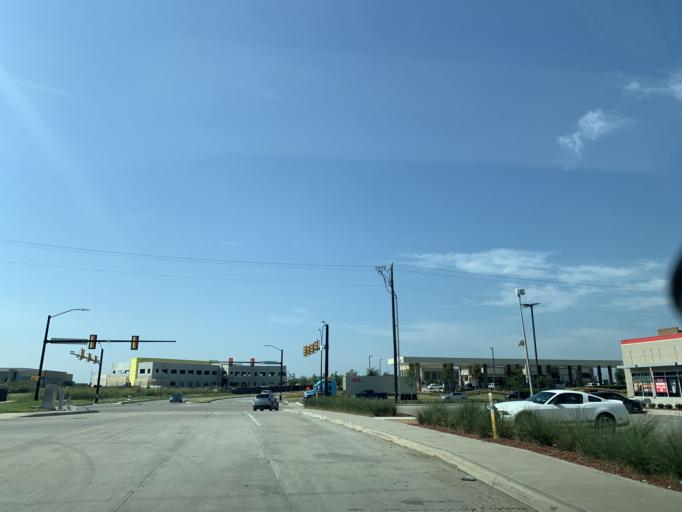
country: US
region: Texas
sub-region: Tarrant County
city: Haslet
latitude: 32.9341
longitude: -97.3119
